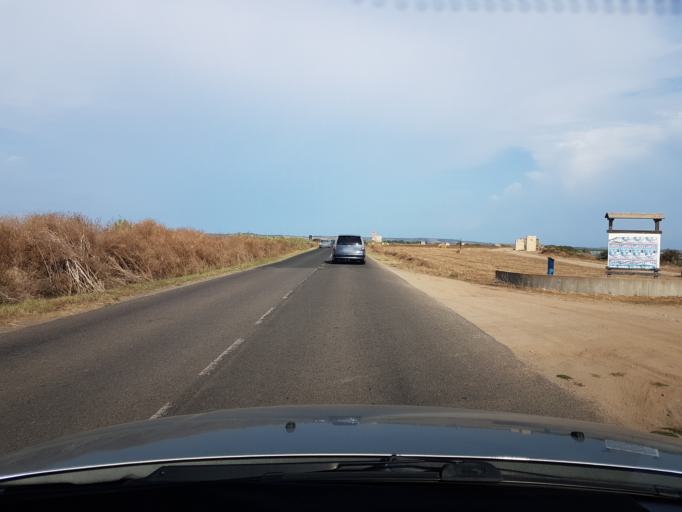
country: IT
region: Sardinia
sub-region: Provincia di Oristano
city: Cabras
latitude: 39.9180
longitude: 8.5169
